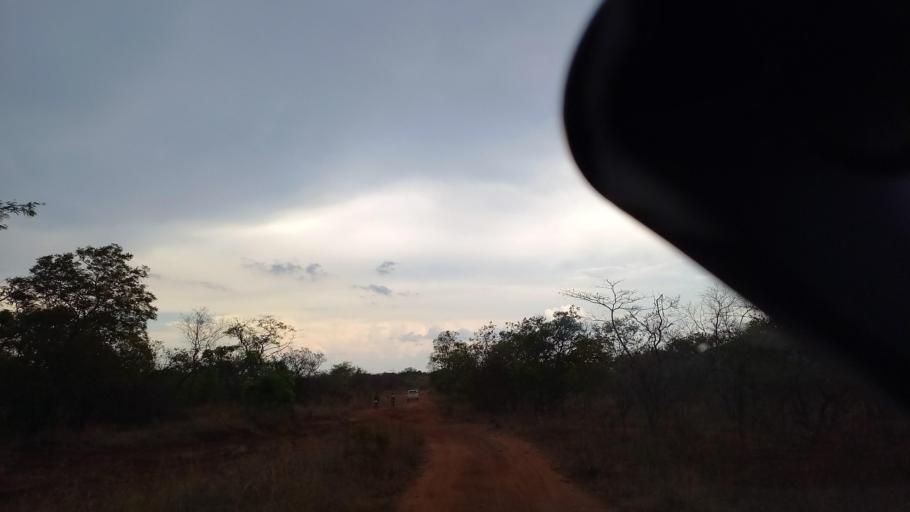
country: ZM
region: Lusaka
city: Kafue
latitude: -15.9986
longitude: 28.2784
